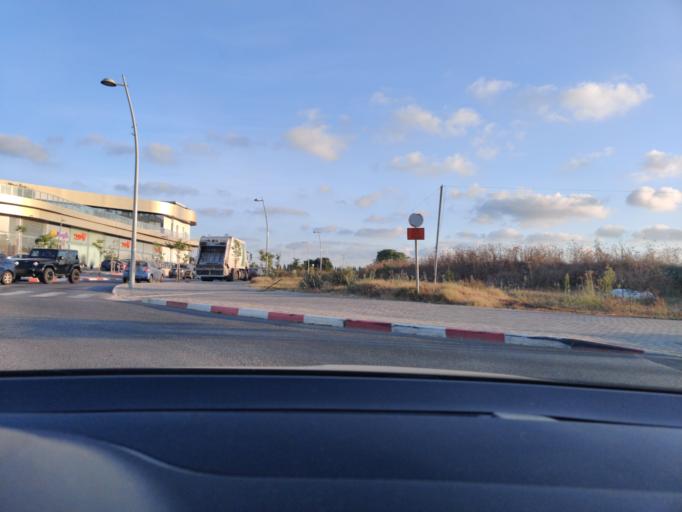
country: IL
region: Central District
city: Elyakhin
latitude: 32.4279
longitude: 34.9327
